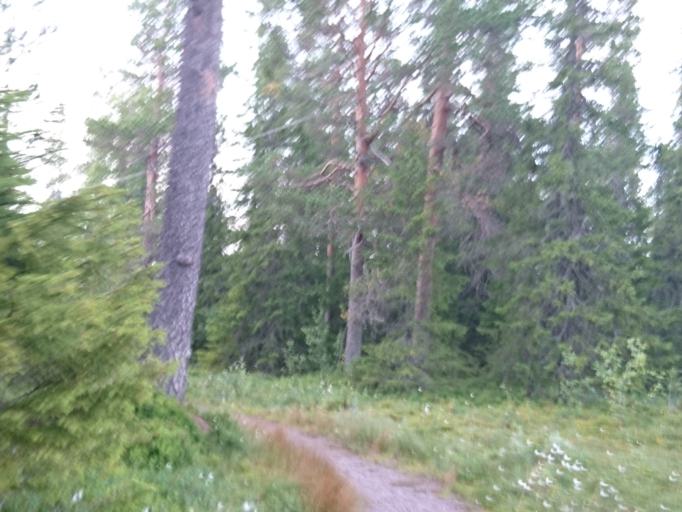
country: SE
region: Dalarna
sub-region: Malung-Saelens kommun
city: Malung
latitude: 61.1717
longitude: 13.1828
